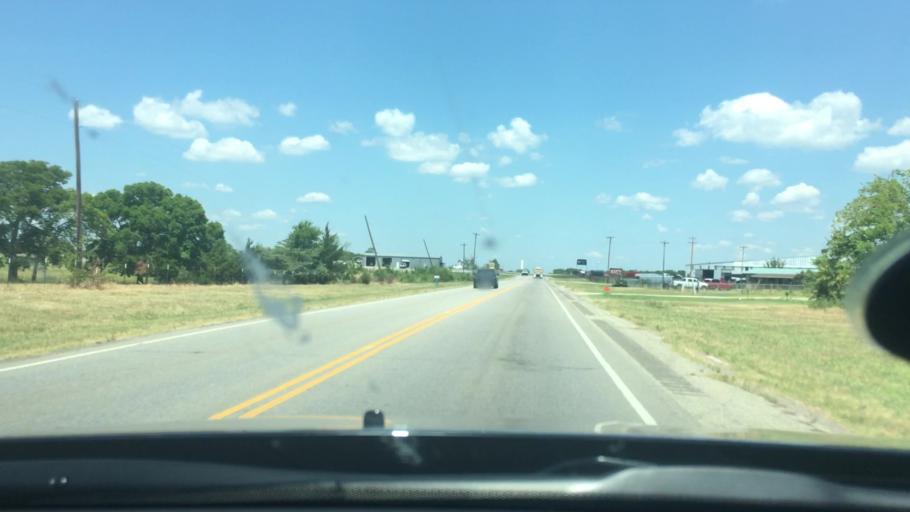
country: US
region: Oklahoma
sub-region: Marshall County
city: Oakland
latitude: 34.1275
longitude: -96.7879
